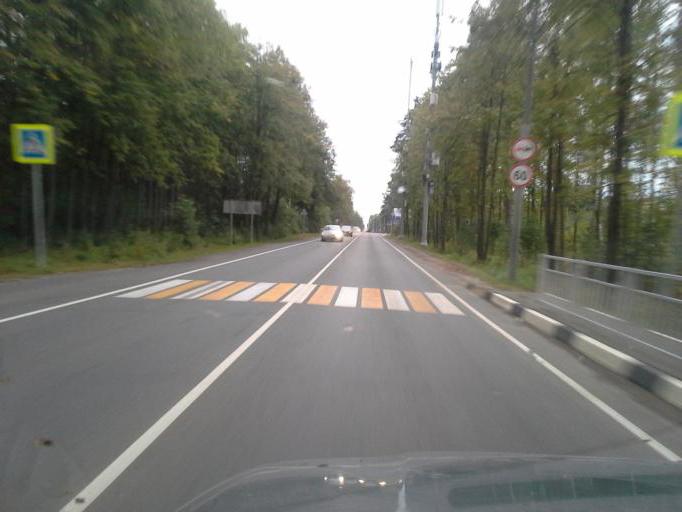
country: RU
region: Moskovskaya
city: Nazar'yevo
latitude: 55.6978
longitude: 37.0654
